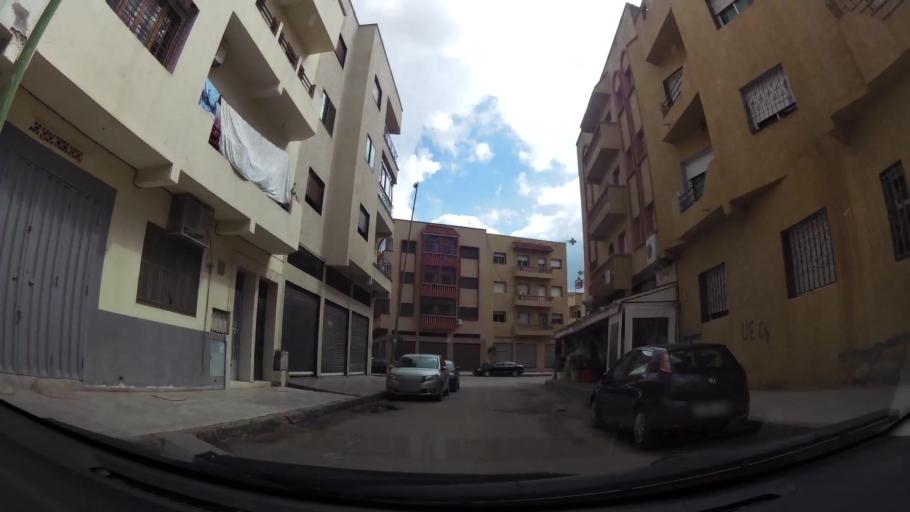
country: MA
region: Chaouia-Ouardigha
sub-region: Settat Province
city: Berrechid
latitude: 33.2749
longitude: -7.5888
